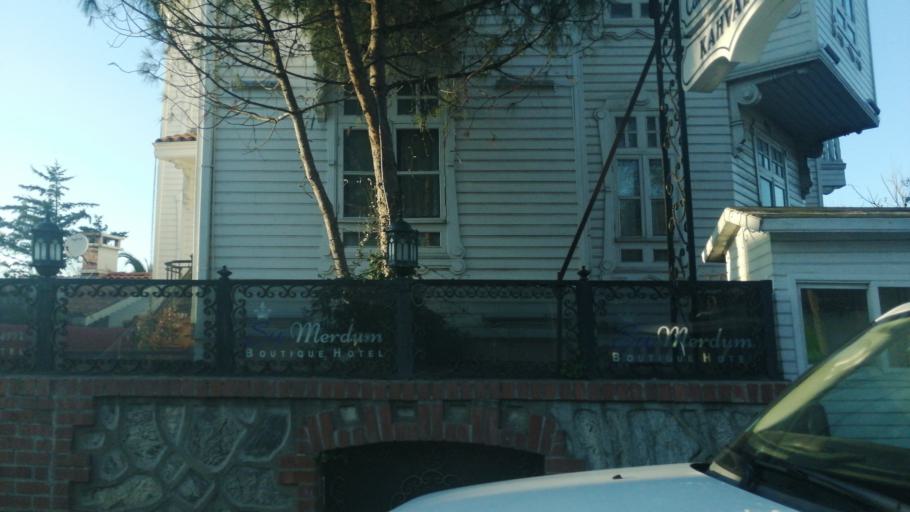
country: TR
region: Istanbul
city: UEskuedar
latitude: 41.0463
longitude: 29.0497
